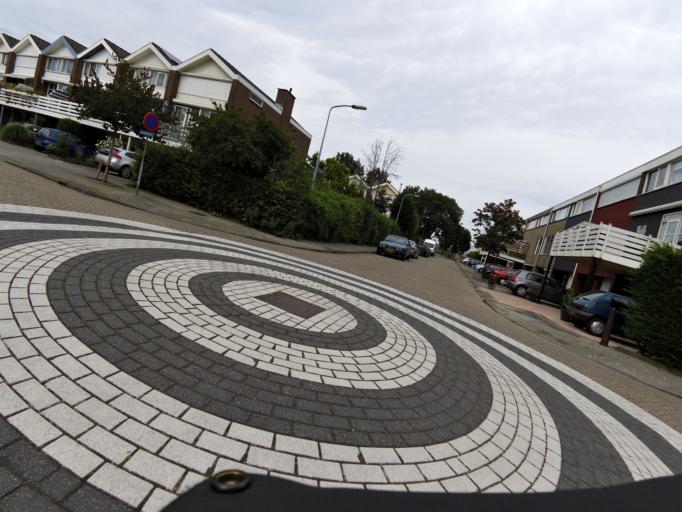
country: NL
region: South Holland
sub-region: Gemeente Goeree-Overflakkee
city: Middelharnis
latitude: 51.6907
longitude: 4.2202
